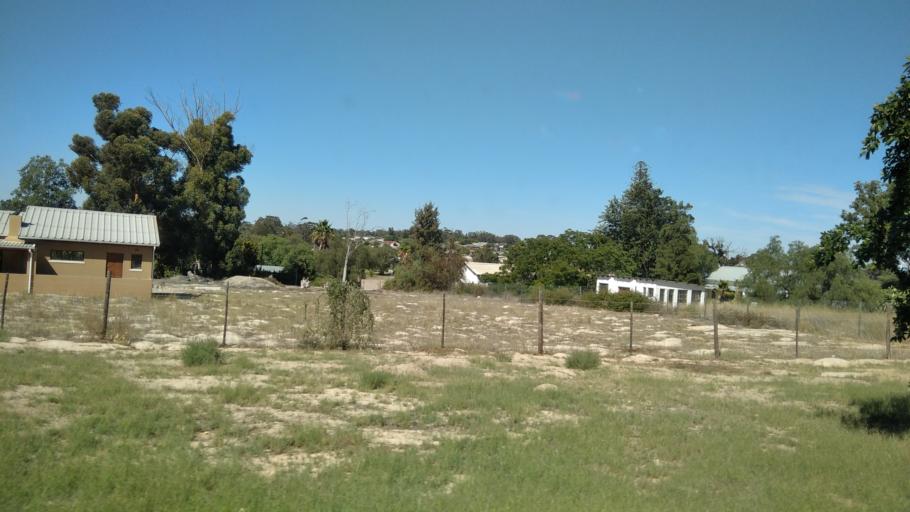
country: ZA
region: Western Cape
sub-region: West Coast District Municipality
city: Moorreesburg
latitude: -33.0578
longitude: 18.3426
